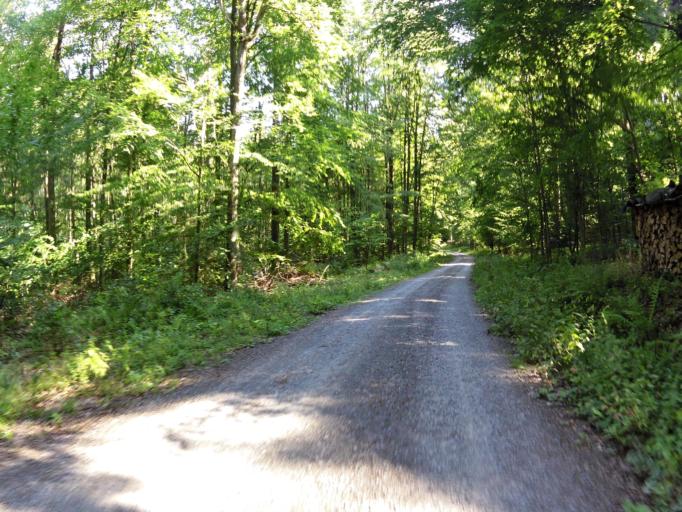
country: DE
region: Bavaria
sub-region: Regierungsbezirk Unterfranken
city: Guntersleben
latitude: 49.8594
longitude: 9.8805
